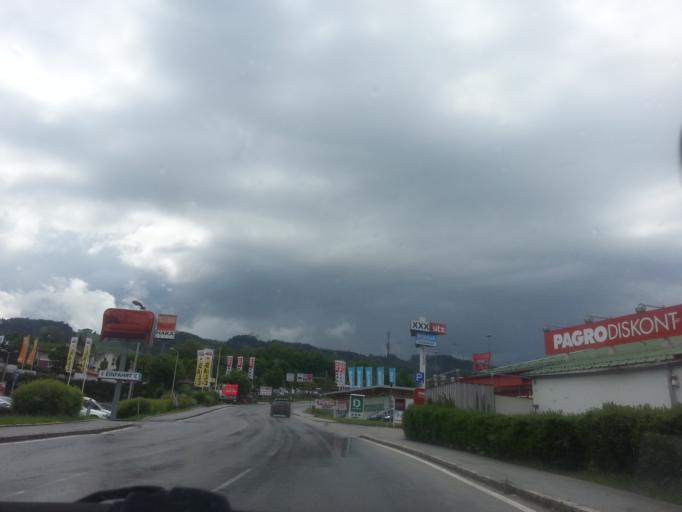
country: AT
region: Salzburg
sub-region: Politischer Bezirk Salzburg-Umgebung
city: Eugendorf
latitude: 47.8585
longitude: 13.1255
